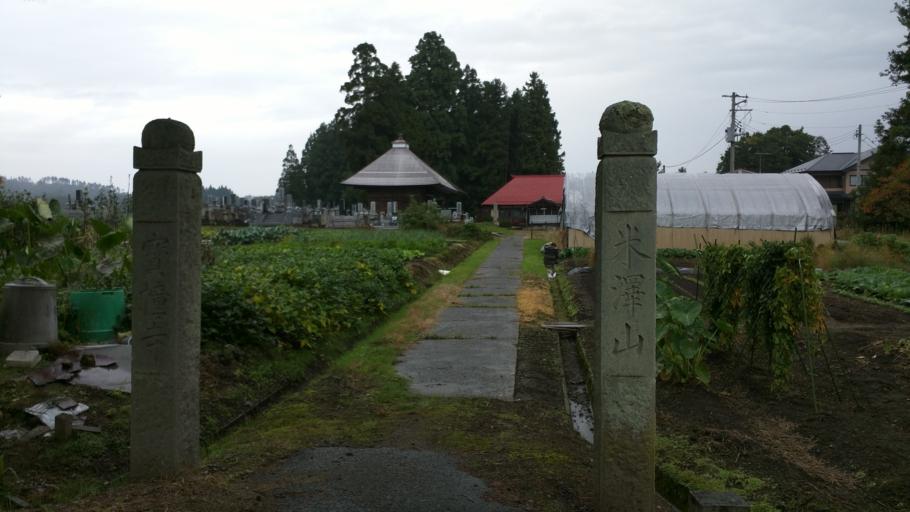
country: JP
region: Fukushima
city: Kitakata
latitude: 37.4938
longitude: 139.8207
